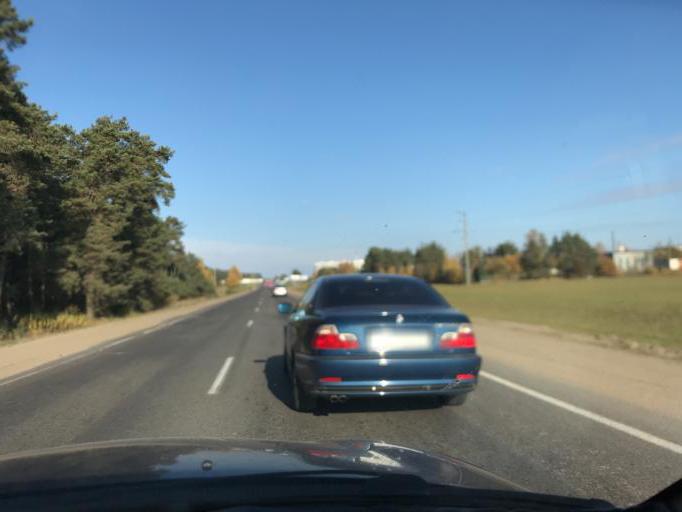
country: BY
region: Grodnenskaya
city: Lida
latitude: 53.8850
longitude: 25.2548
